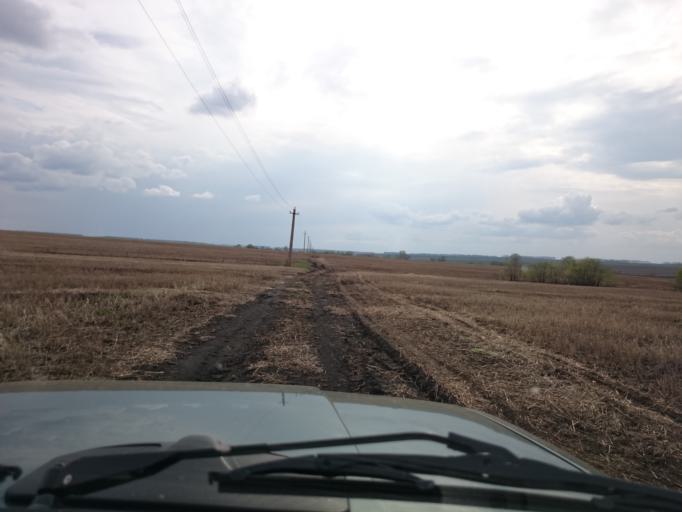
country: RU
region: Mordoviya
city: Kadoshkino
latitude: 54.0210
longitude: 44.4700
